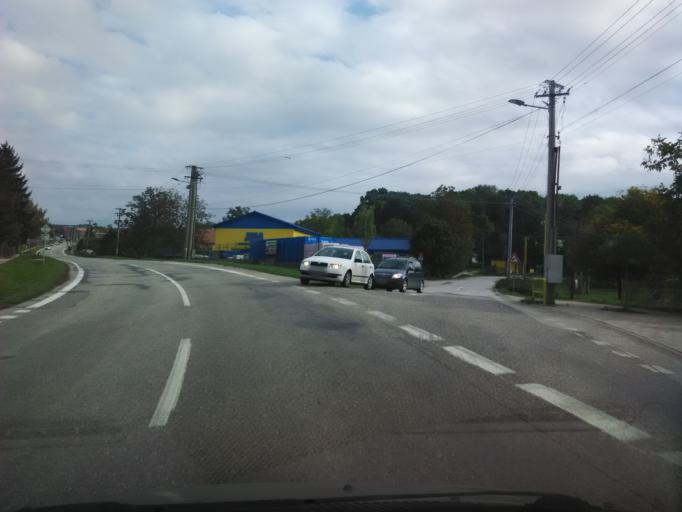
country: SK
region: Nitriansky
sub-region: Okres Nitra
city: Nitra
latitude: 48.2906
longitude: 18.1849
